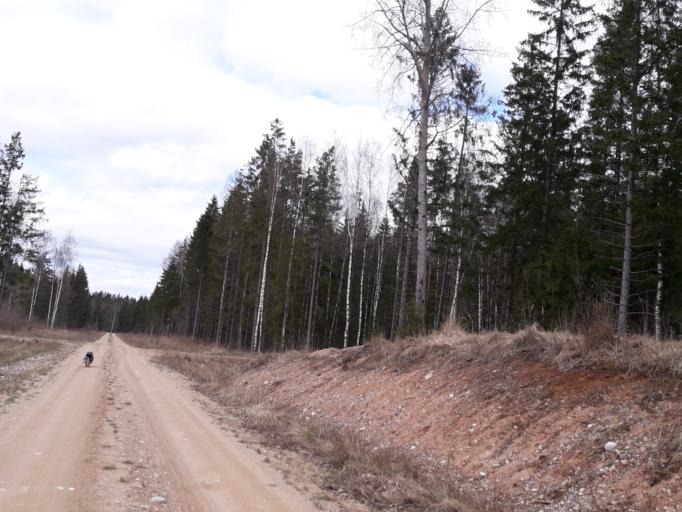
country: LV
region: Broceni
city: Broceni
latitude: 56.8875
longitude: 22.3847
